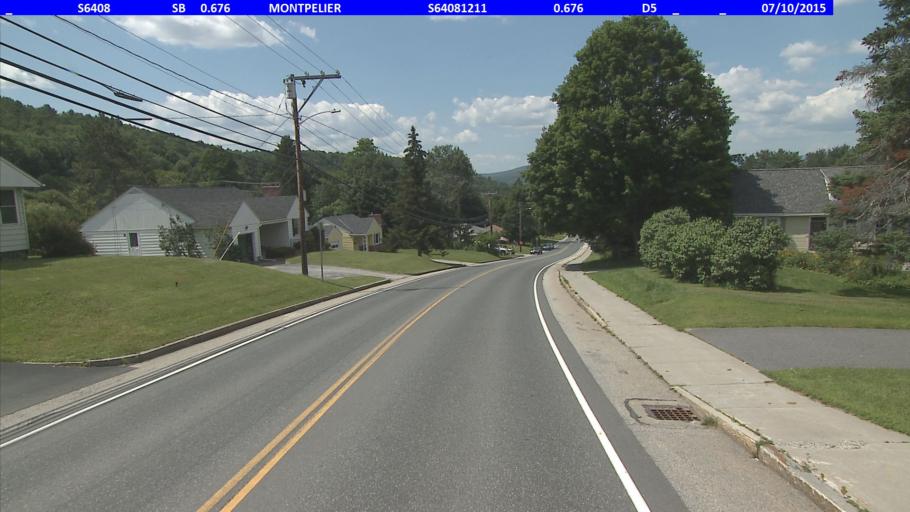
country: US
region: Vermont
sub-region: Washington County
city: Montpelier
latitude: 44.2431
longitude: -72.5647
